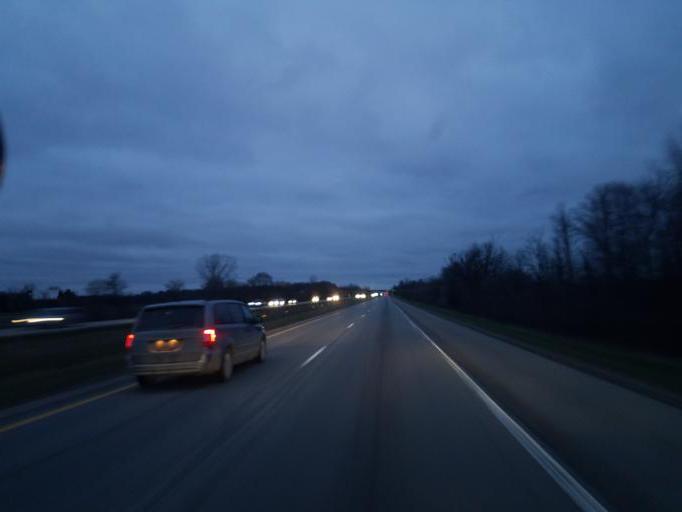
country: US
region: Michigan
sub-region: Washtenaw County
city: Milan
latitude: 42.1264
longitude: -83.6827
